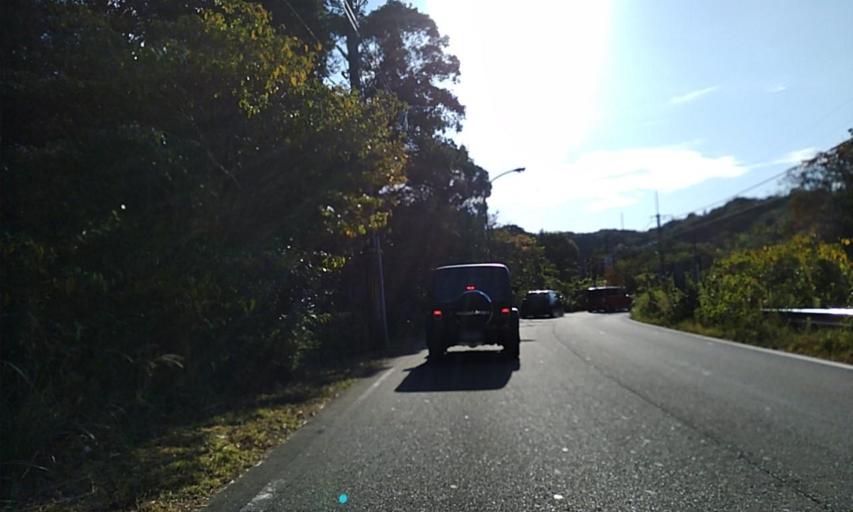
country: JP
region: Wakayama
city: Tanabe
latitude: 33.6822
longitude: 135.3982
